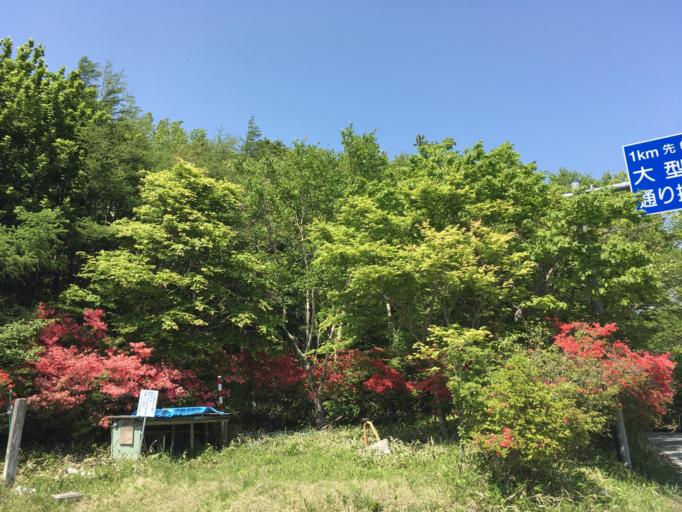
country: JP
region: Iwate
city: Ofunato
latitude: 39.1786
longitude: 141.7420
